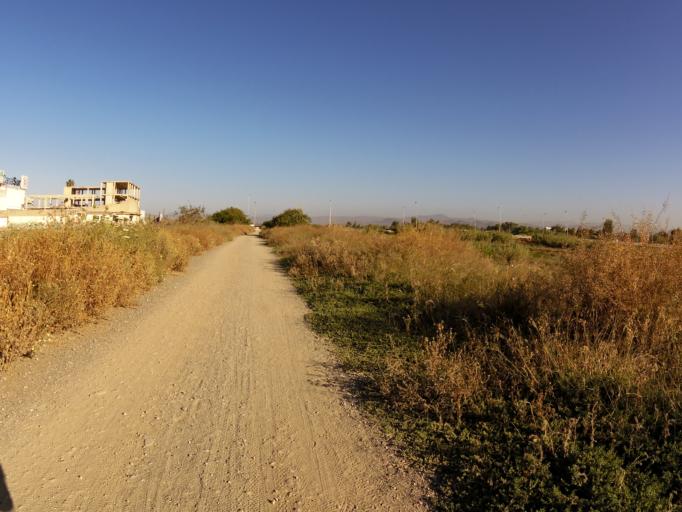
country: ES
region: Andalusia
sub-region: Provincia de Malaga
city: Torremolinos
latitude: 36.6764
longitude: -4.4725
